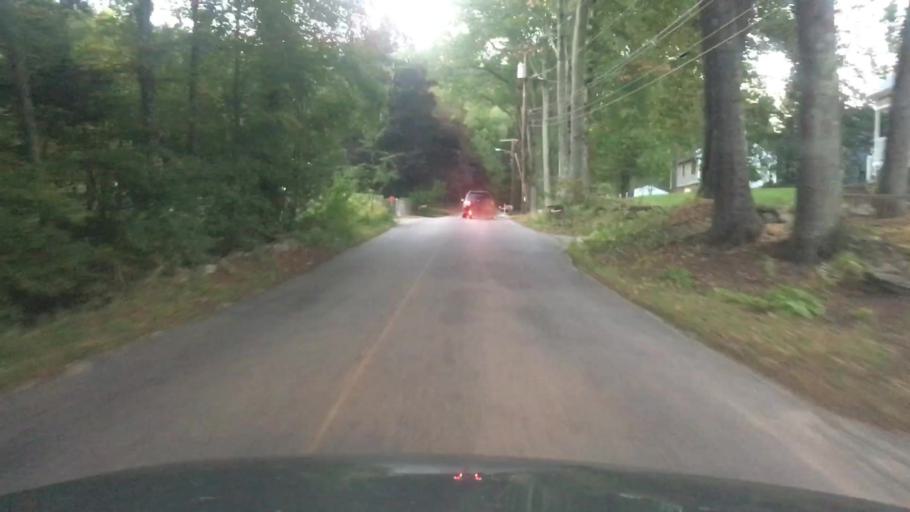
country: US
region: Massachusetts
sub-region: Worcester County
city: Charlton
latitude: 42.1290
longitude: -71.9754
